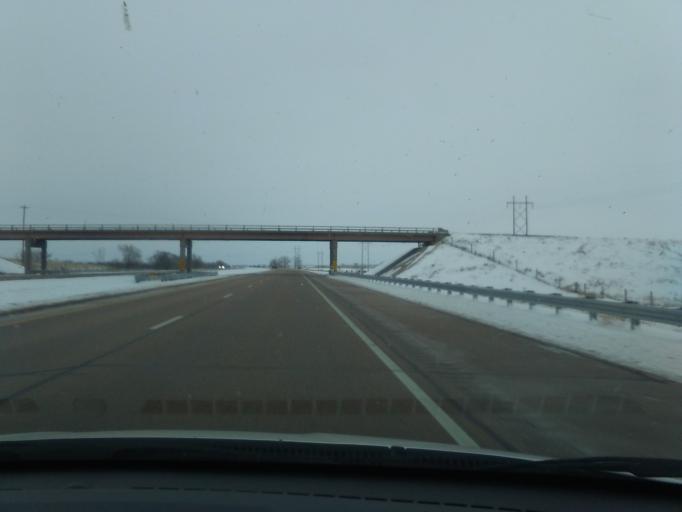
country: US
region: Nebraska
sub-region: Keith County
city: Ogallala
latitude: 41.0955
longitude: -101.8084
